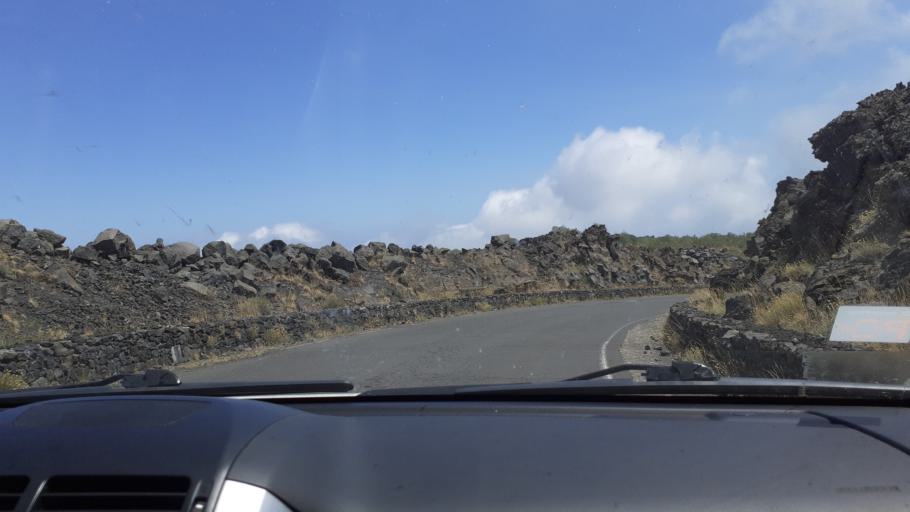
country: IT
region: Sicily
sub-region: Catania
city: Nicolosi
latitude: 37.6879
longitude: 15.0283
